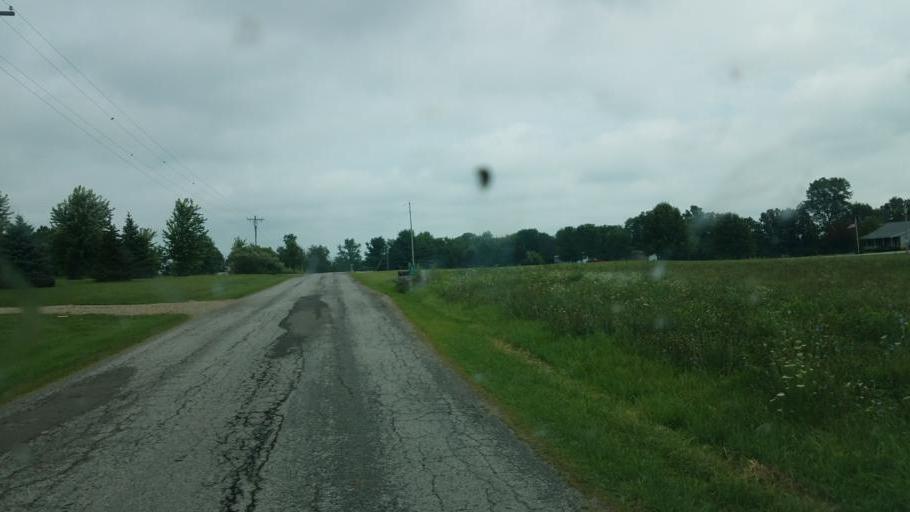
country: US
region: Ohio
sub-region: Morrow County
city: Mount Gilead
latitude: 40.4634
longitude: -82.7625
